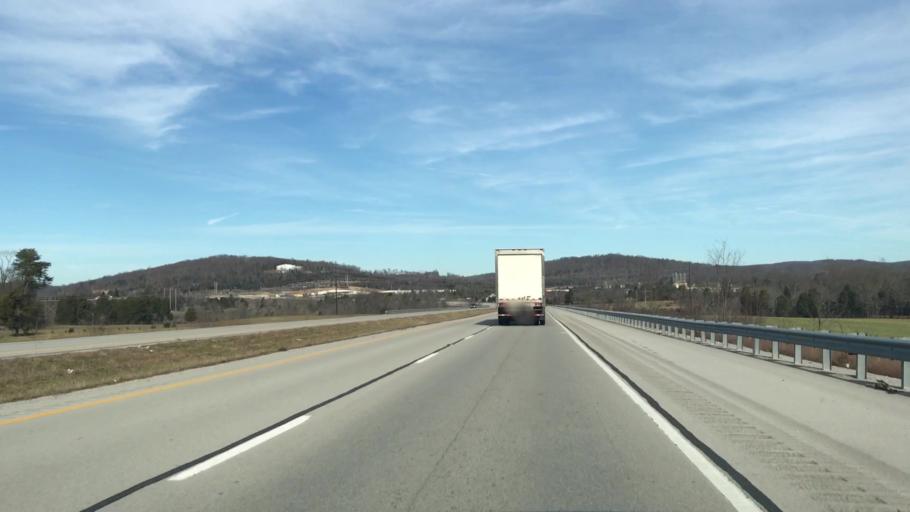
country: US
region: Kentucky
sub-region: Pulaski County
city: Somerset
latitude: 37.0388
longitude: -84.5876
